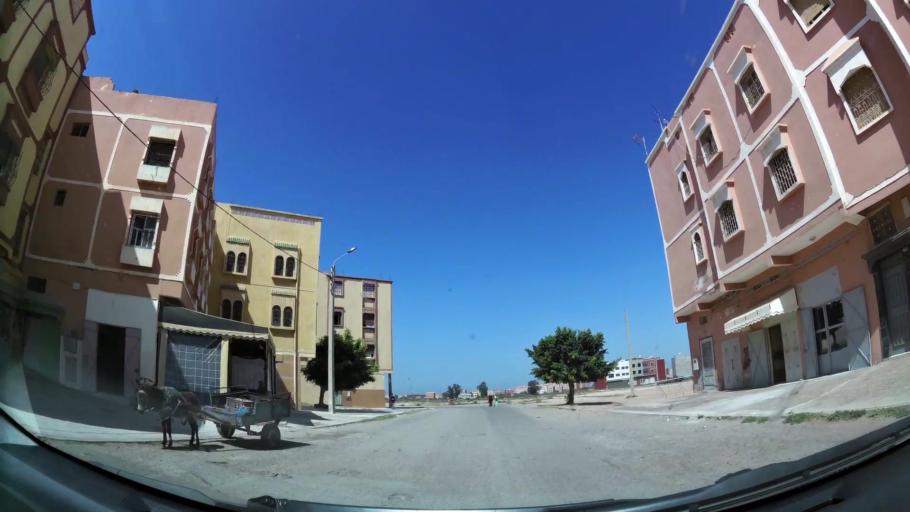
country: MA
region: Souss-Massa-Draa
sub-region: Inezgane-Ait Mellou
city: Inezgane
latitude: 30.3349
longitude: -9.5088
